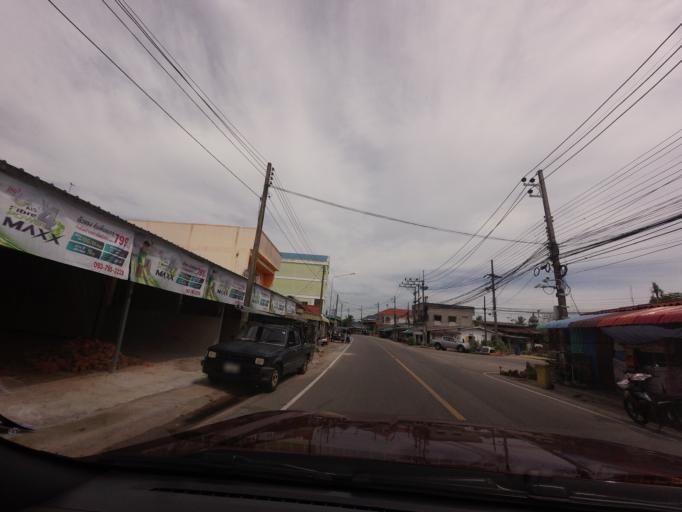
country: TH
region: Narathiwat
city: Tak Bai
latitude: 6.2380
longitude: 102.0867
